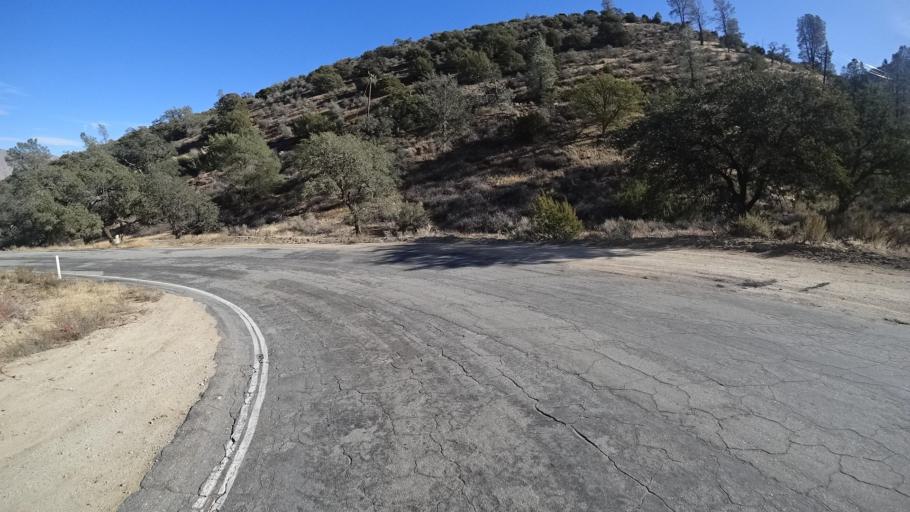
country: US
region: California
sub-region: Kern County
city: Bodfish
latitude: 35.5756
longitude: -118.5040
